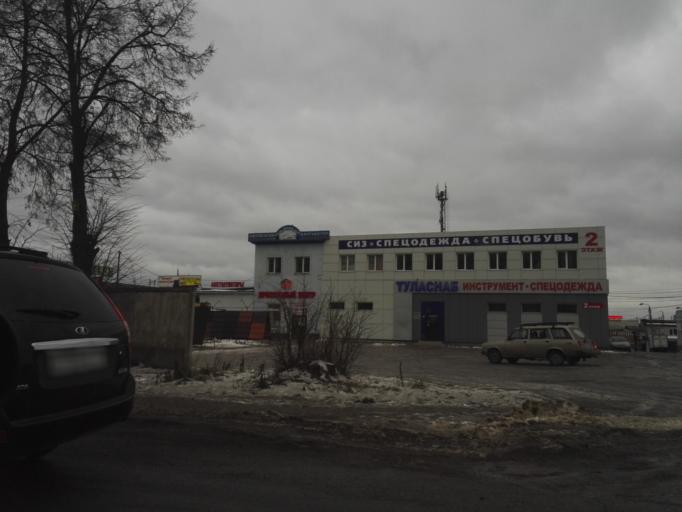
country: RU
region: Tula
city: Tula
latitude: 54.1606
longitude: 37.6367
